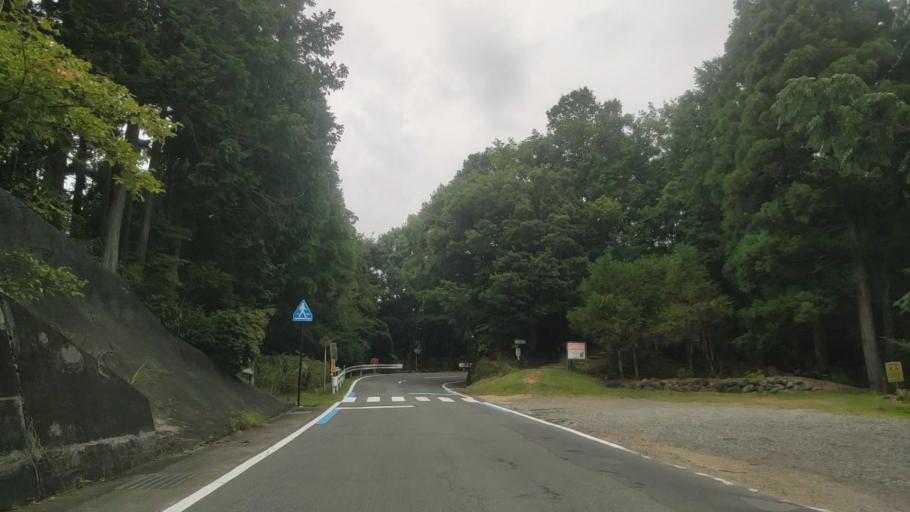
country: JP
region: Wakayama
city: Koya
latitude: 34.2167
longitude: 135.5503
